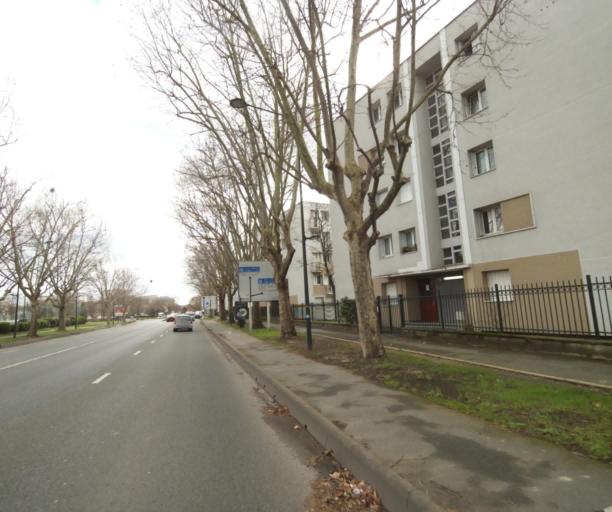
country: FR
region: Ile-de-France
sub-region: Departement de Seine-Saint-Denis
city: Saint-Denis
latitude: 48.9406
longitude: 2.3673
